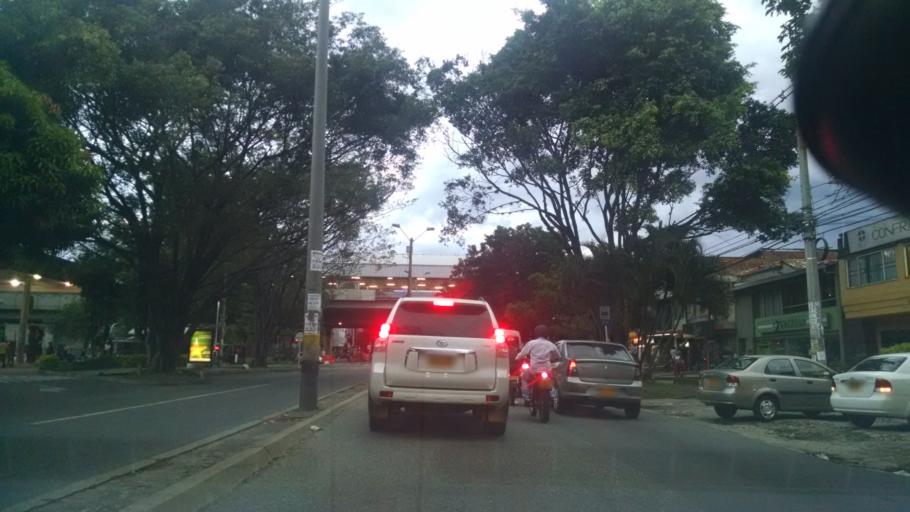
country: CO
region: Antioquia
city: Medellin
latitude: 6.2597
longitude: -75.5976
